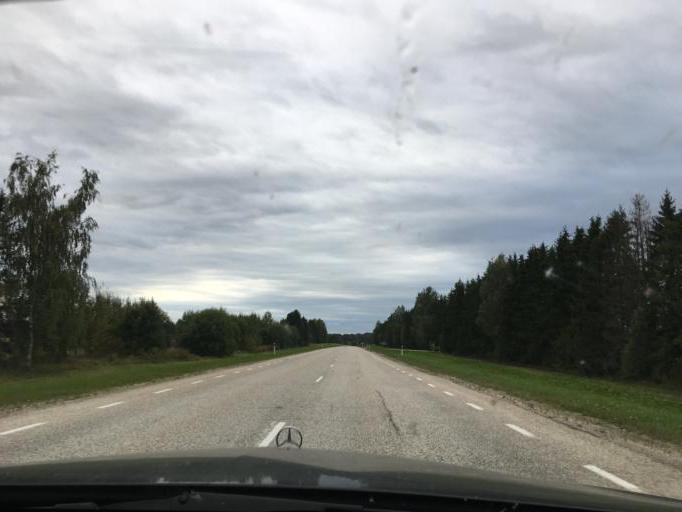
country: LV
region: Aluksnes Rajons
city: Aluksne
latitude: 57.6168
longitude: 27.2671
